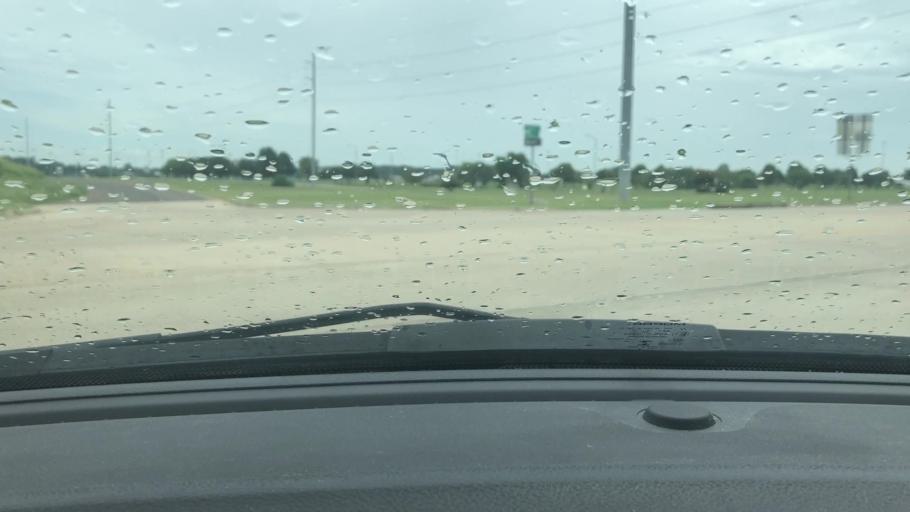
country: US
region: Texas
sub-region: Bowie County
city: Wake Village
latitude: 33.3868
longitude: -94.0939
